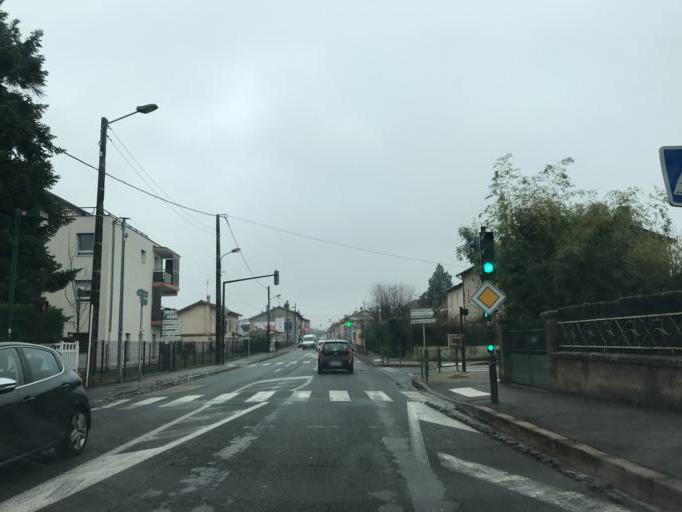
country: FR
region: Rhone-Alpes
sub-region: Departement de l'Ain
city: Villars-les-Dombes
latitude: 46.0018
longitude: 5.0309
